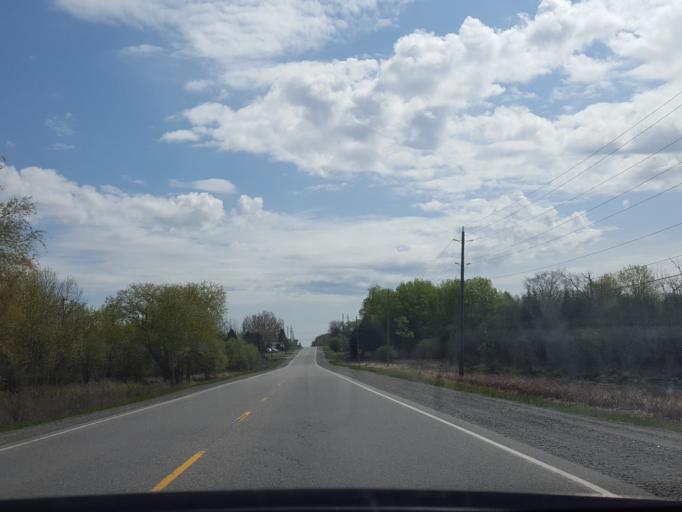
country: CA
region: Ontario
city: Oshawa
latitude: 44.1077
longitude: -78.8734
